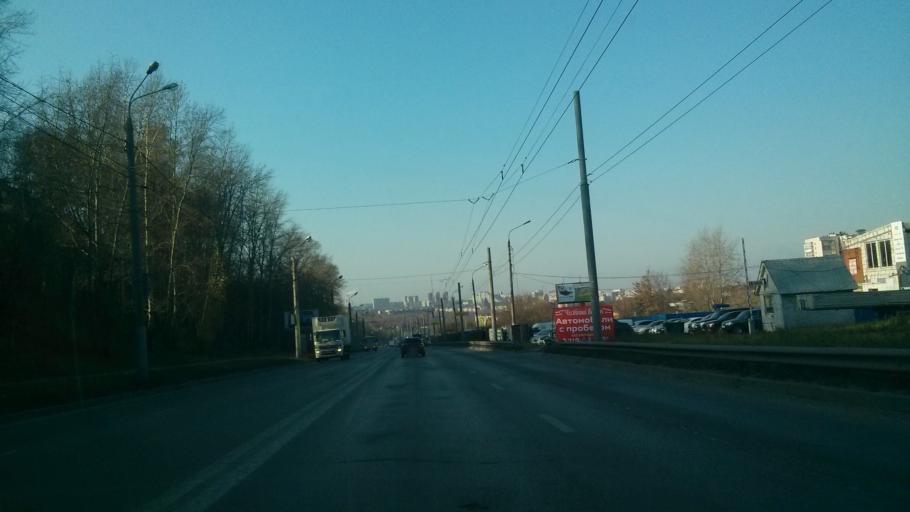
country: RU
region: Nizjnij Novgorod
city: Afonino
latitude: 56.2993
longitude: 44.0746
